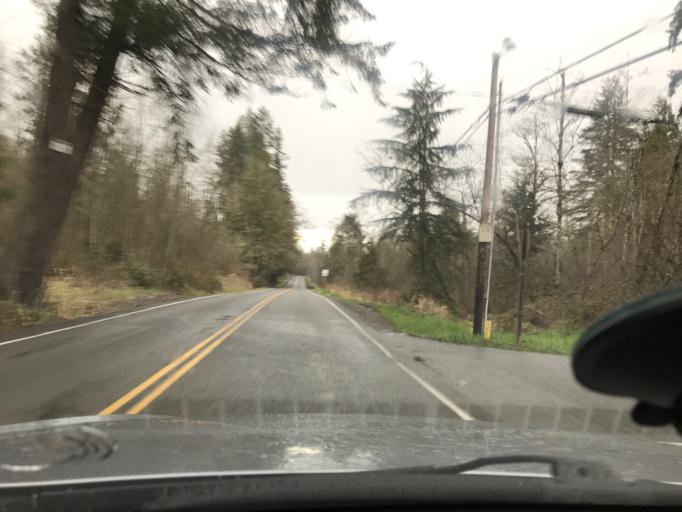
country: US
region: Washington
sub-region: King County
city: Ames Lake
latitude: 47.6525
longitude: -121.9630
